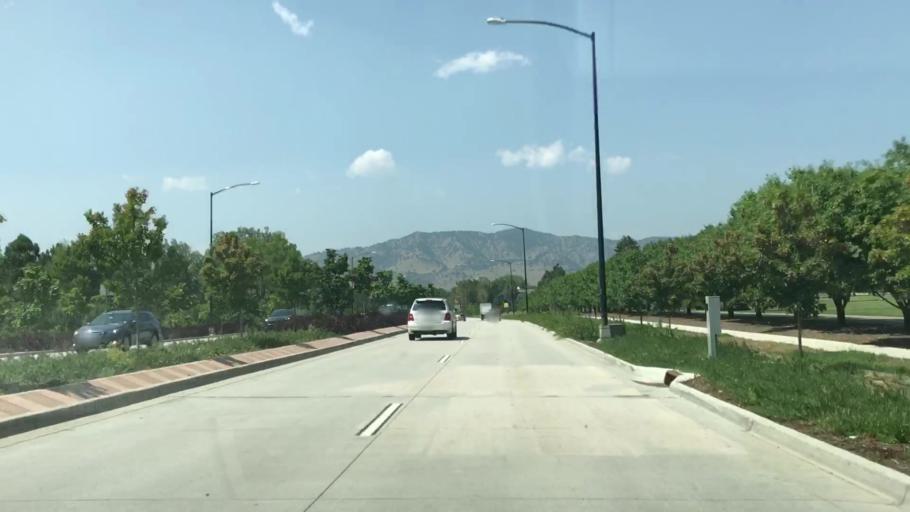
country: US
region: Colorado
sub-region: Boulder County
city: Boulder
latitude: 40.0382
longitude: -105.2495
